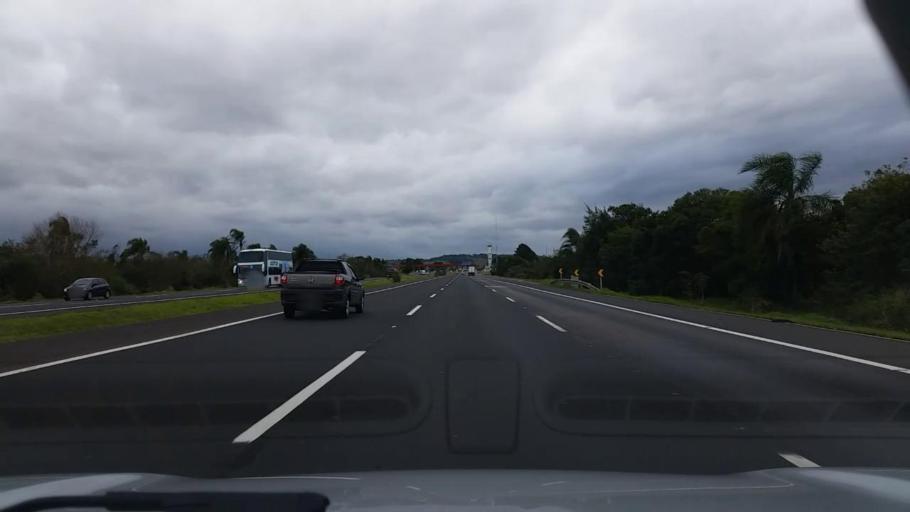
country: BR
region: Rio Grande do Sul
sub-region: Osorio
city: Osorio
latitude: -29.8833
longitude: -50.4412
